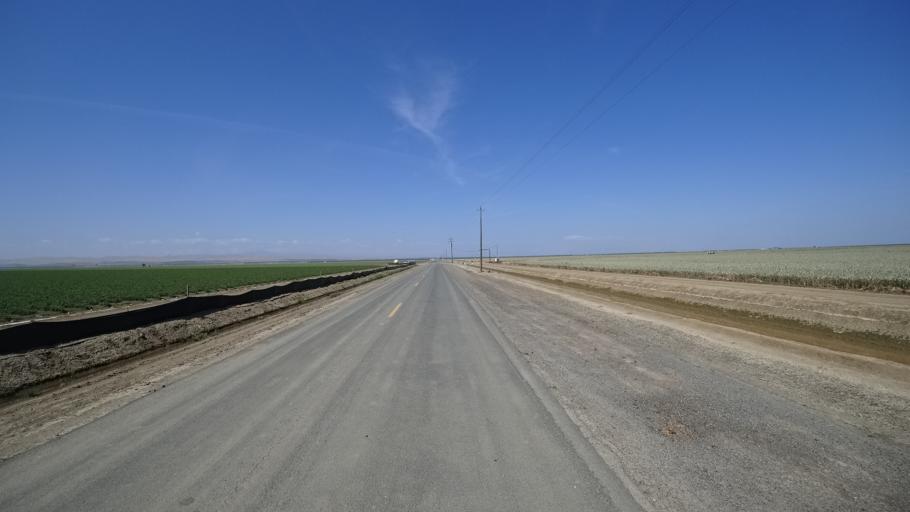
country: US
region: California
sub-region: Kings County
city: Kettleman City
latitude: 36.0941
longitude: -119.9390
